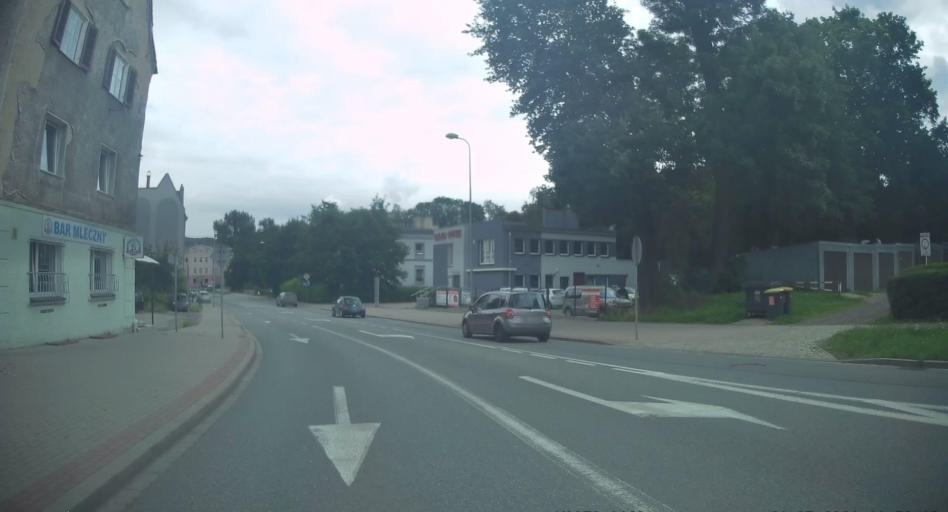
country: PL
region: Lower Silesian Voivodeship
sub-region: Powiat walbrzyski
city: Walbrzych
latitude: 50.7832
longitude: 16.2872
